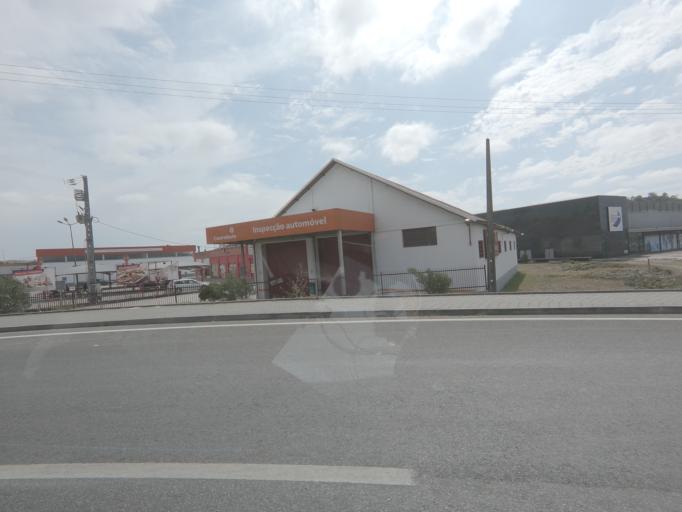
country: PT
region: Leiria
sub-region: Leiria
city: Leiria
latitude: 39.7472
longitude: -8.8203
